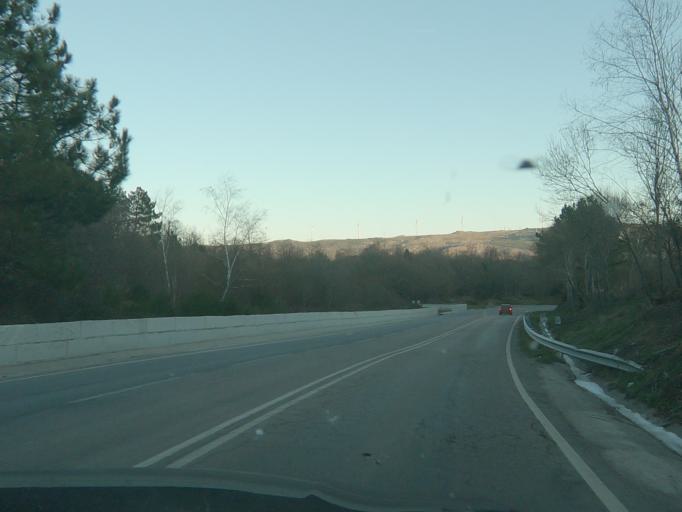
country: PT
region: Vila Real
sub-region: Vila Pouca de Aguiar
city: Vila Pouca de Aguiar
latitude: 41.4903
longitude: -7.6678
